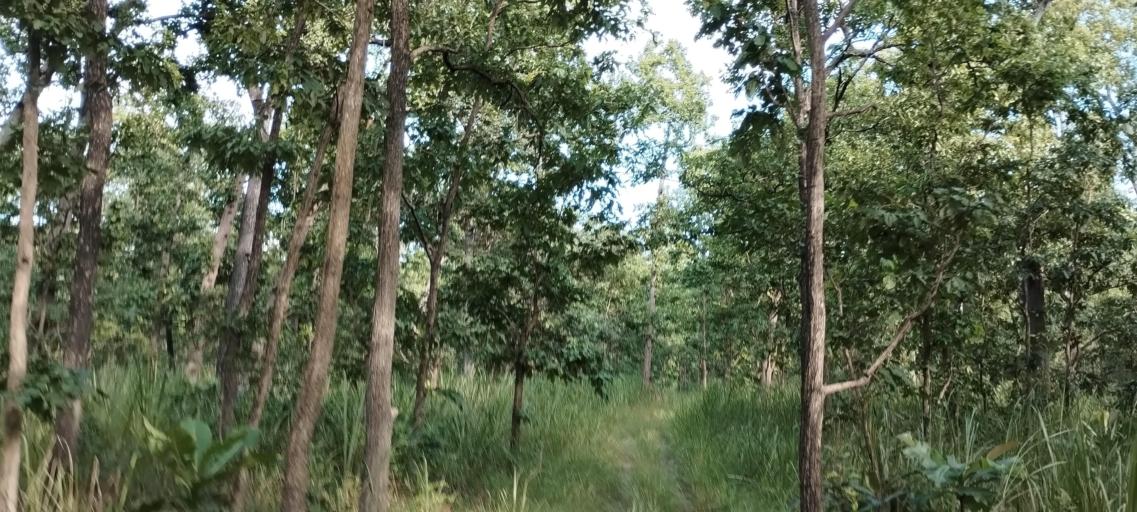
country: NP
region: Far Western
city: Tikapur
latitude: 28.5511
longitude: 81.2844
